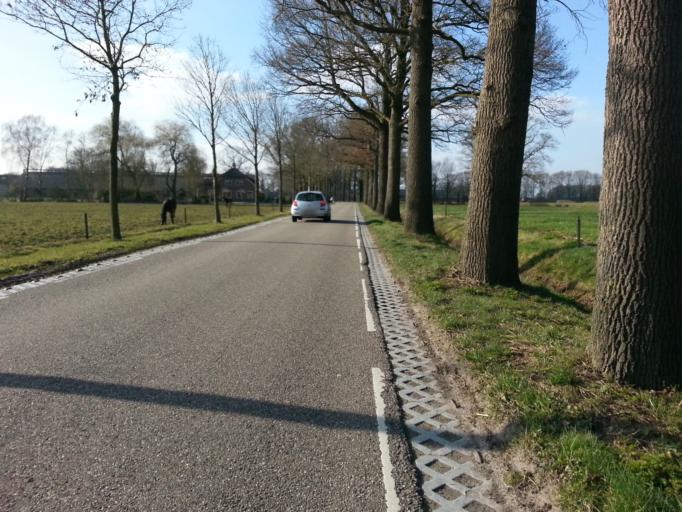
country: NL
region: Utrecht
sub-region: Gemeente Woudenberg
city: Woudenberg
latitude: 52.0892
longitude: 5.4576
